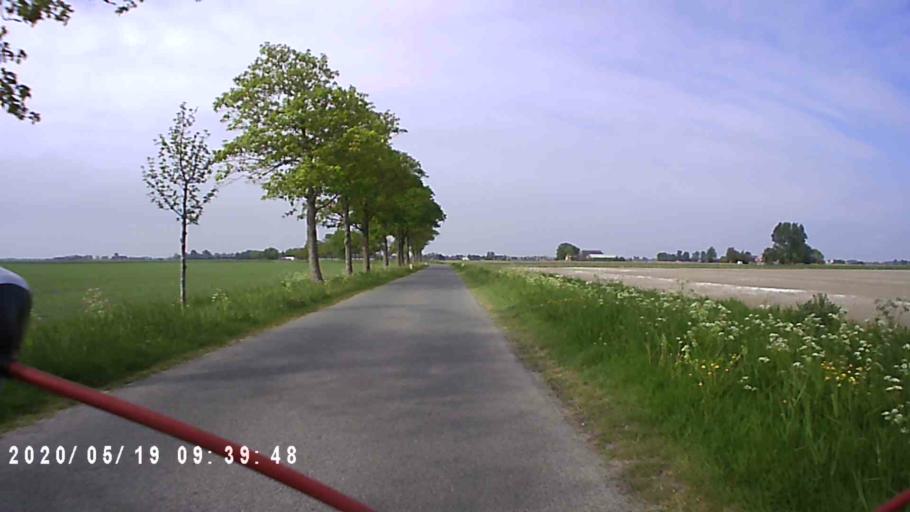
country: NL
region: Groningen
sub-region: Gemeente Zuidhorn
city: Grijpskerk
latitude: 53.2880
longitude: 6.2782
